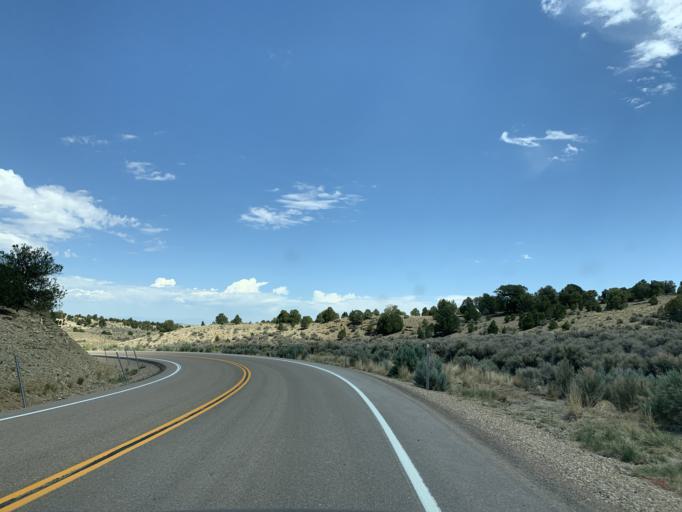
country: US
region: Utah
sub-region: Duchesne County
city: Duchesne
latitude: 39.8929
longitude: -110.2399
